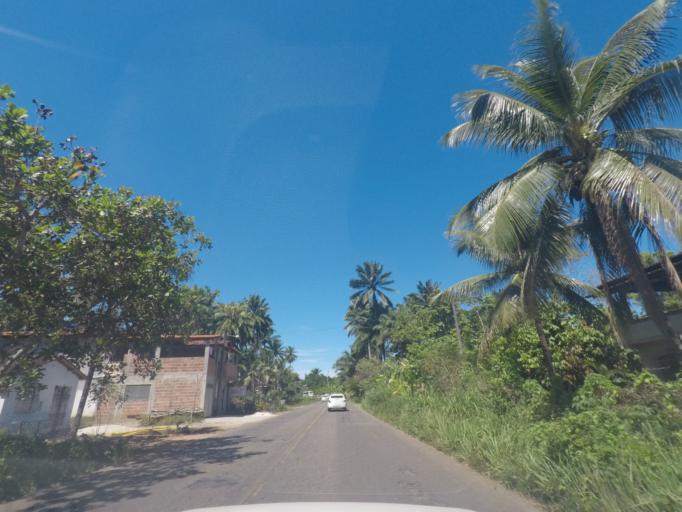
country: BR
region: Bahia
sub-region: Valenca
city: Valenca
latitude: -13.4433
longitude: -39.0817
